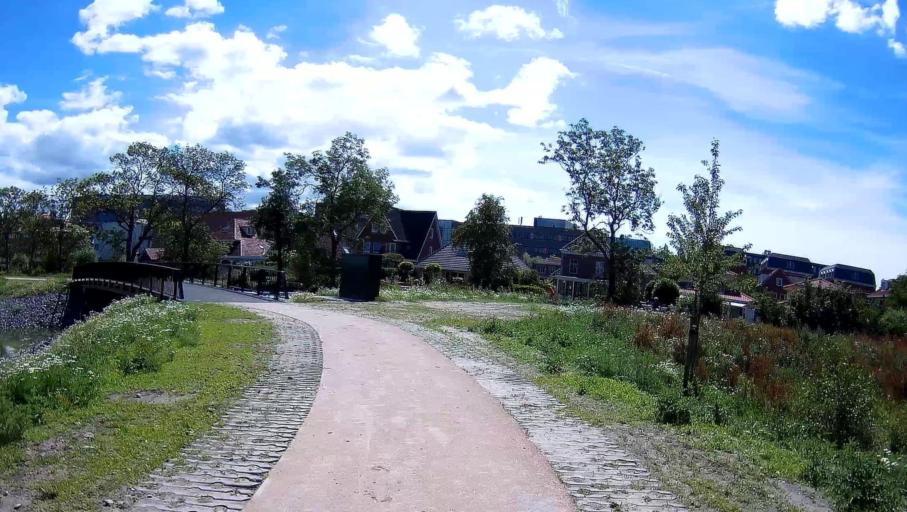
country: NL
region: South Holland
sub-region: Gemeente Leidschendam-Voorburg
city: Voorburg
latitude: 52.0531
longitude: 4.3484
